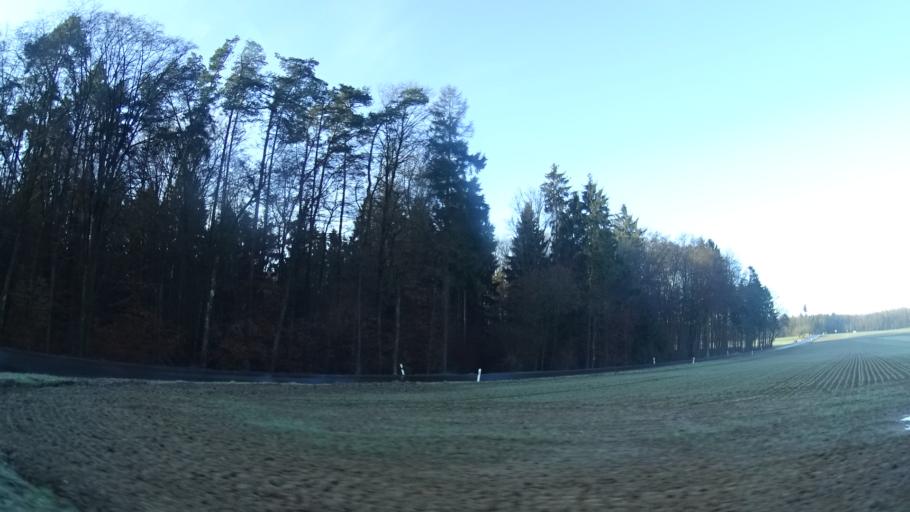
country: DE
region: Bavaria
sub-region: Regierungsbezirk Unterfranken
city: Neunkirchen
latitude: 49.7314
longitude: 9.3900
